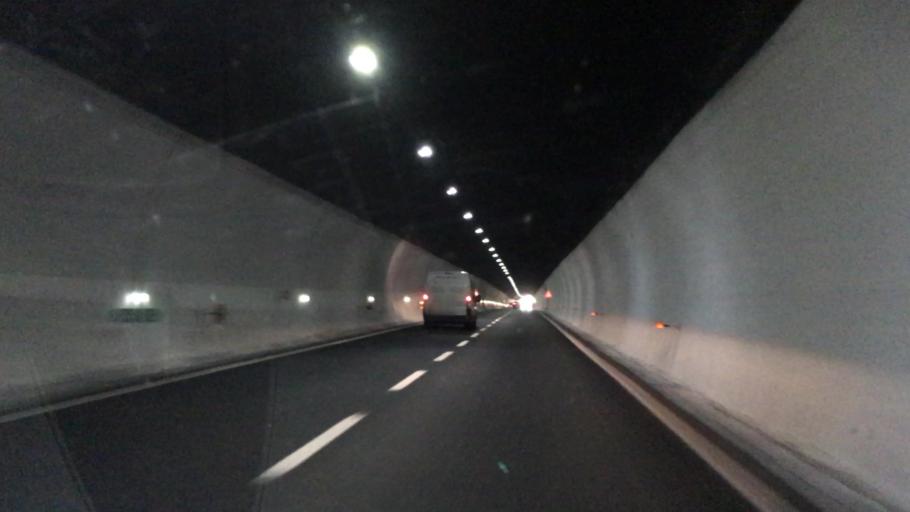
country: IT
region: Liguria
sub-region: Provincia di Genova
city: Cogorno
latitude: 44.3026
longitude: 9.3739
